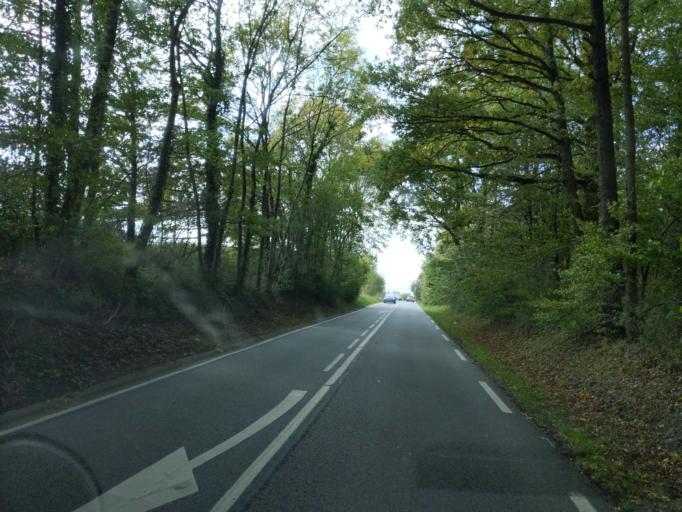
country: FR
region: Ile-de-France
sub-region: Departement des Yvelines
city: Dampierre-en-Yvelines
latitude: 48.6855
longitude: 2.0073
